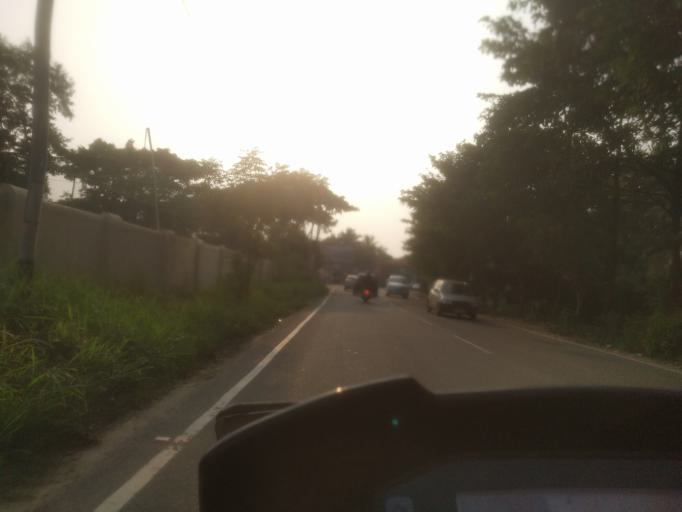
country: IN
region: Kerala
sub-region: Alappuzha
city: Arukutti
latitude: 9.9417
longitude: 76.3409
